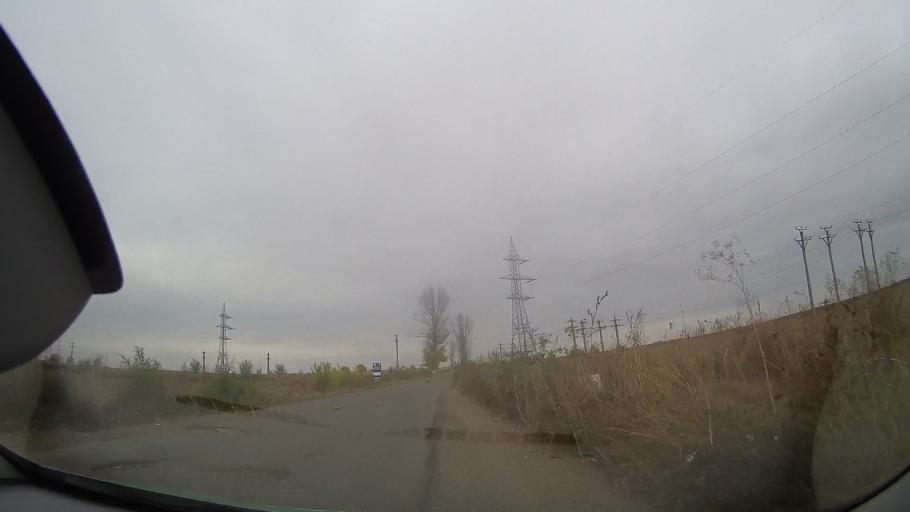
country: RO
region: Braila
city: Dudesti
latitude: 44.8974
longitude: 27.4331
